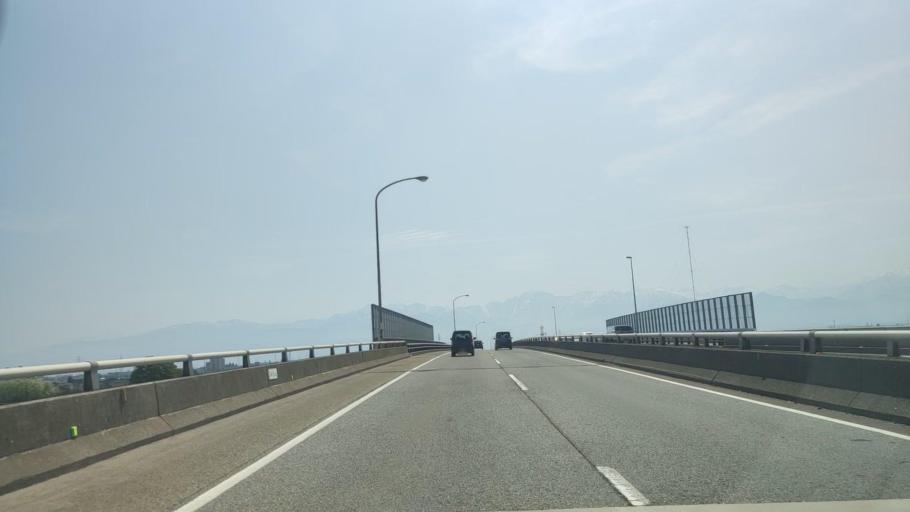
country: JP
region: Toyama
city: Toyama-shi
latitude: 36.7237
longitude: 137.2414
